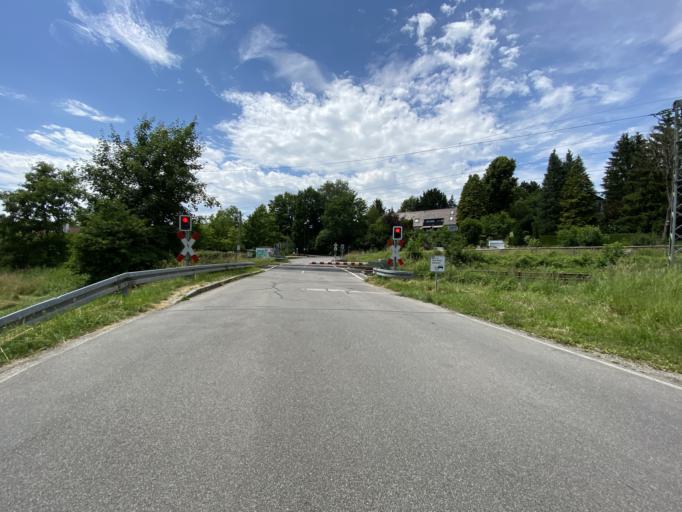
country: DE
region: Bavaria
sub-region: Upper Bavaria
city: Seefeld
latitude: 48.0430
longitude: 11.2009
